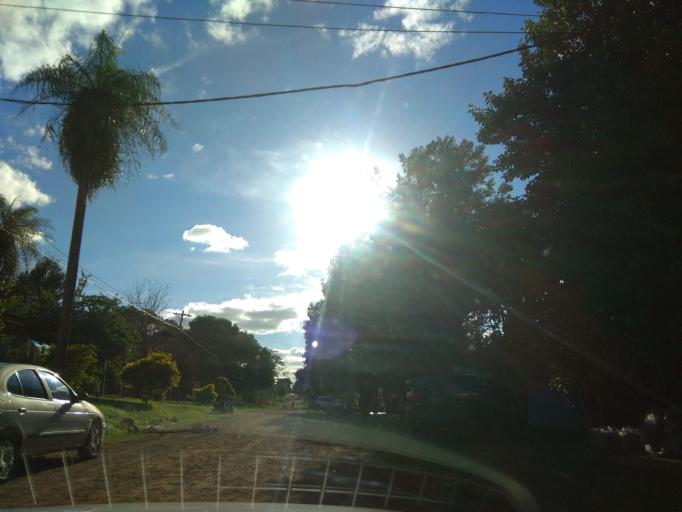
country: AR
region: Misiones
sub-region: Departamento de Capital
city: Posadas
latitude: -27.3958
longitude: -55.9281
